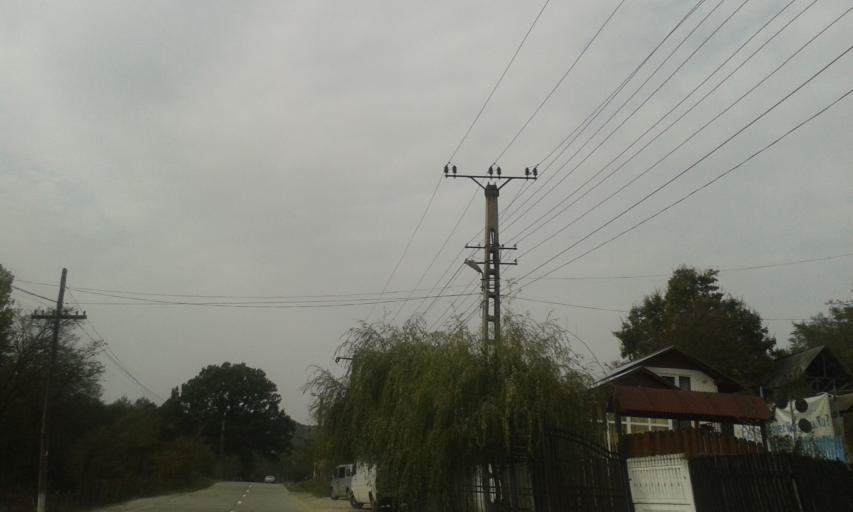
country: RO
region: Valcea
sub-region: Comuna Gradistea
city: Gradistea
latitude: 44.9111
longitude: 23.7859
